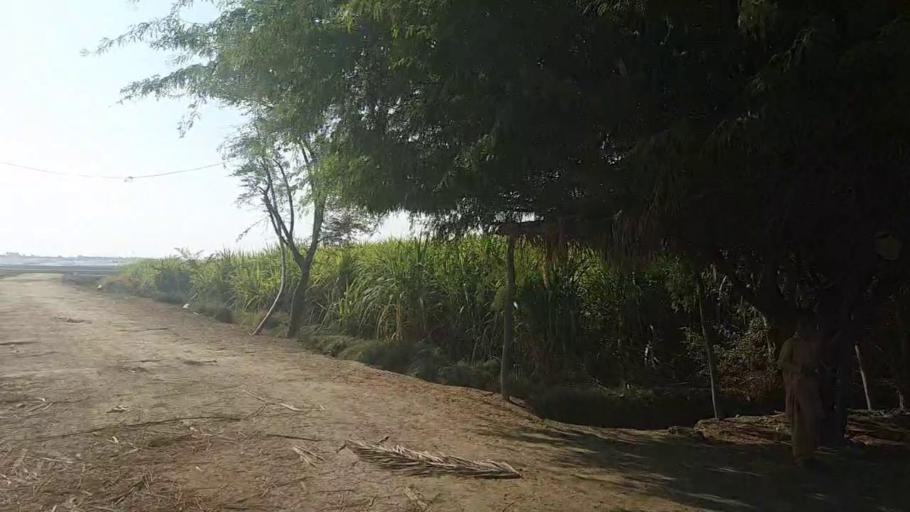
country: PK
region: Sindh
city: Khairpur
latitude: 27.4410
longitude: 68.7290
